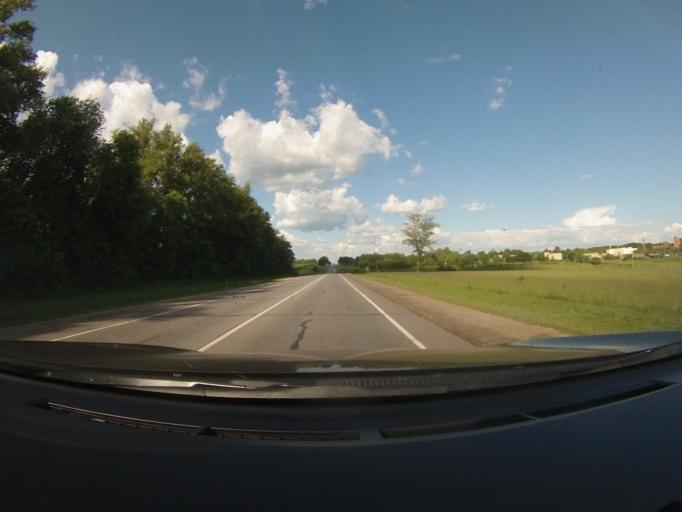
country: RU
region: Tula
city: Bol'shoye Skuratovo
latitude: 53.4419
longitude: 36.8291
